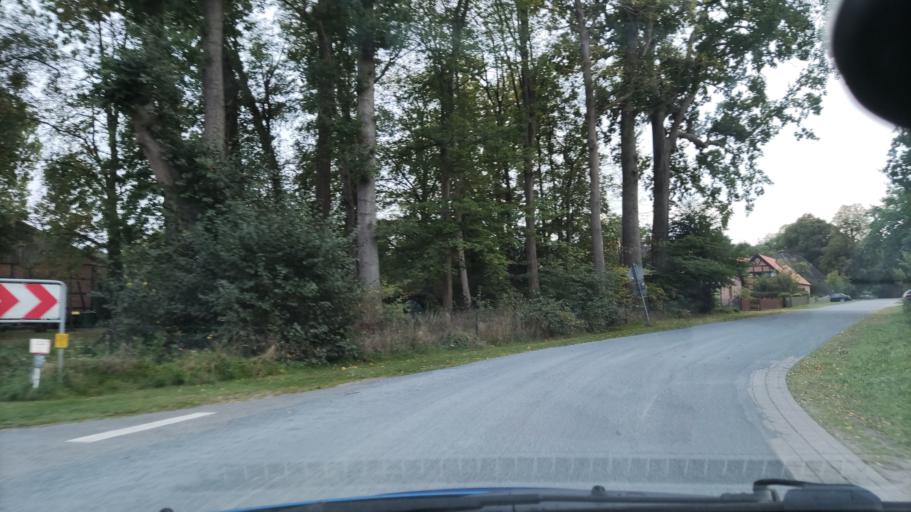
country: DE
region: Lower Saxony
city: Karwitz
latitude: 53.0890
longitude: 11.0176
